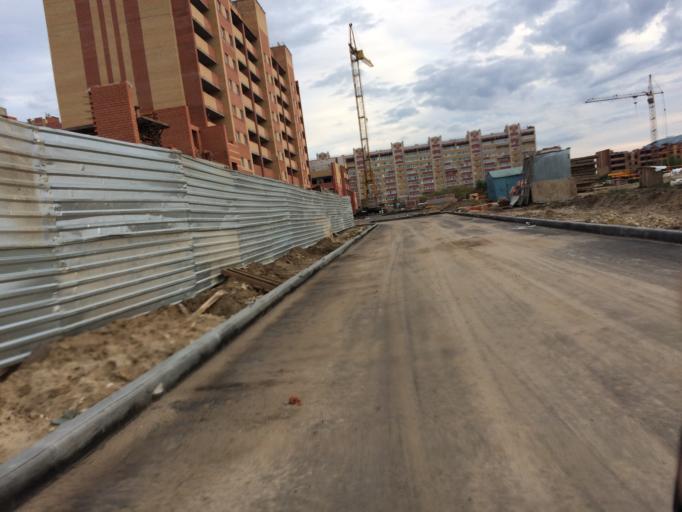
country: RU
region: Mariy-El
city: Yoshkar-Ola
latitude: 56.6430
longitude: 47.9233
